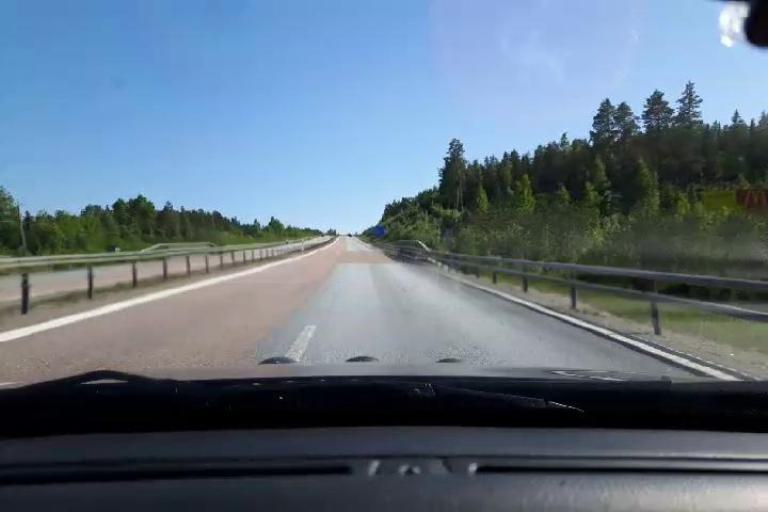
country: SE
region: Gaevleborg
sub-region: Soderhamns Kommun
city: Soderhamn
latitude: 61.3524
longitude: 17.0168
